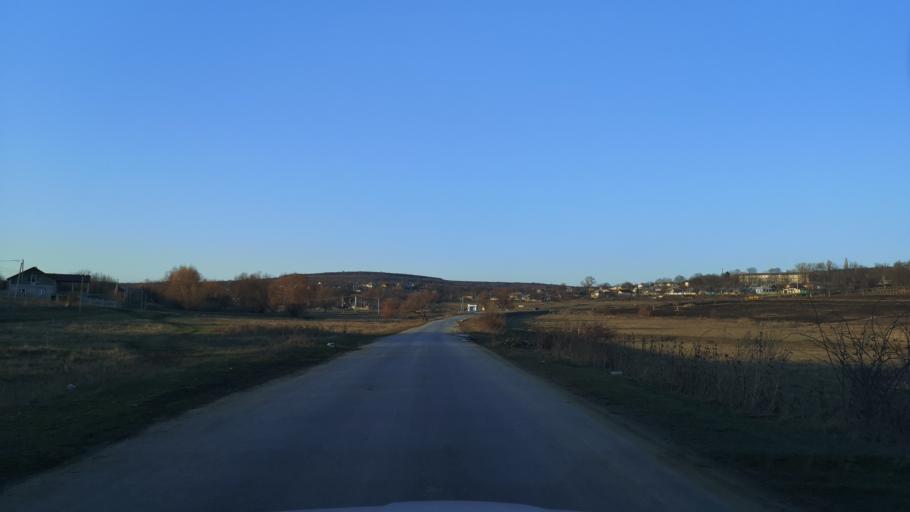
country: MD
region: Orhei
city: Orhei
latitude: 47.3506
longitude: 28.6957
